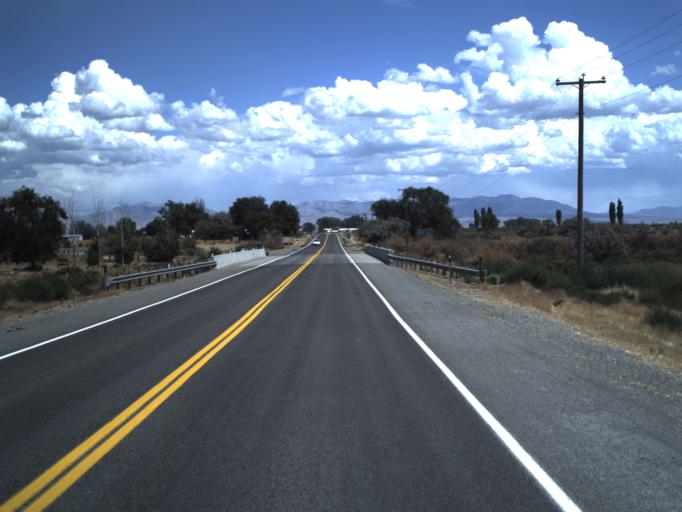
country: US
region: Utah
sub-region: Millard County
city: Delta
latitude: 39.3305
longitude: -112.6227
